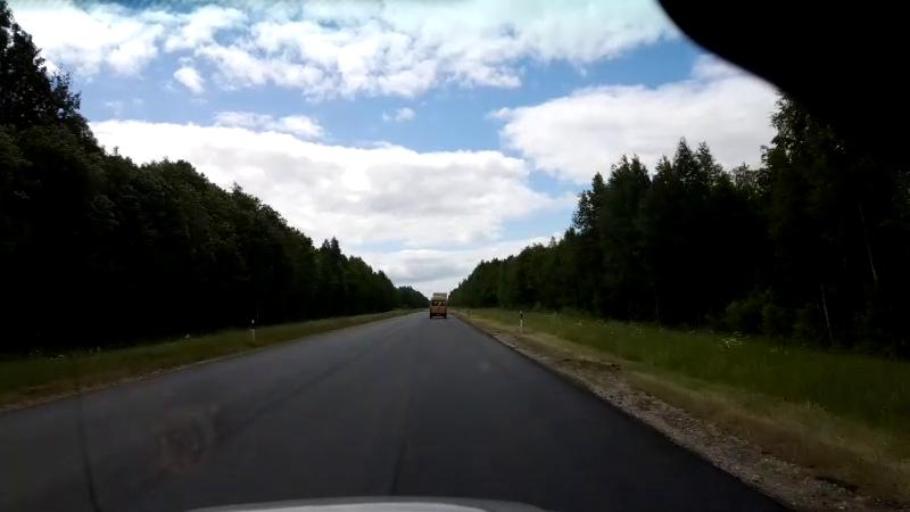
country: LV
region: Salacgrivas
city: Ainazi
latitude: 57.9242
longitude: 24.4242
